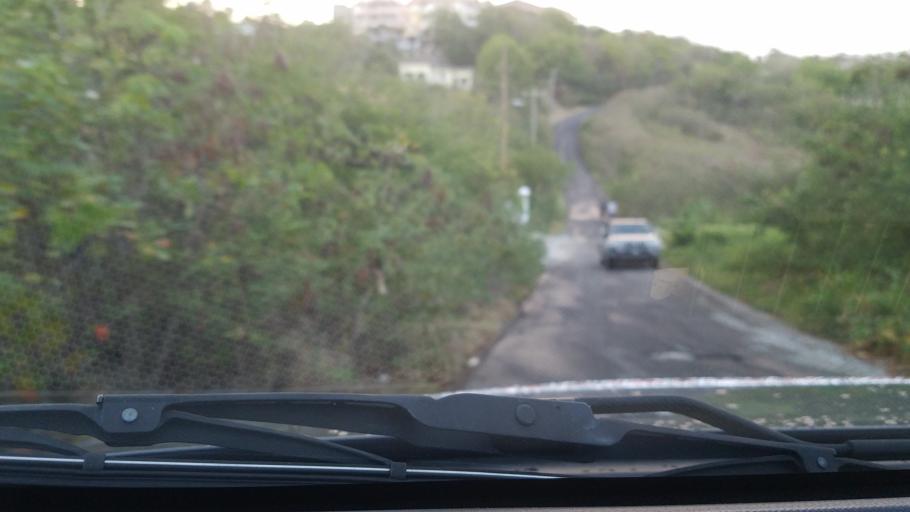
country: LC
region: Gros-Islet
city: Gros Islet
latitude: 14.0911
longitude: -60.9402
